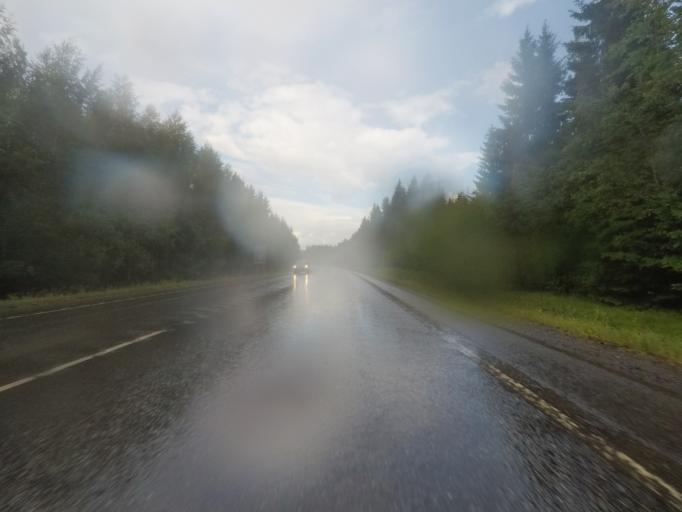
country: FI
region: Southern Savonia
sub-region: Mikkeli
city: Mikkeli
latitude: 61.6446
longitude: 27.0968
